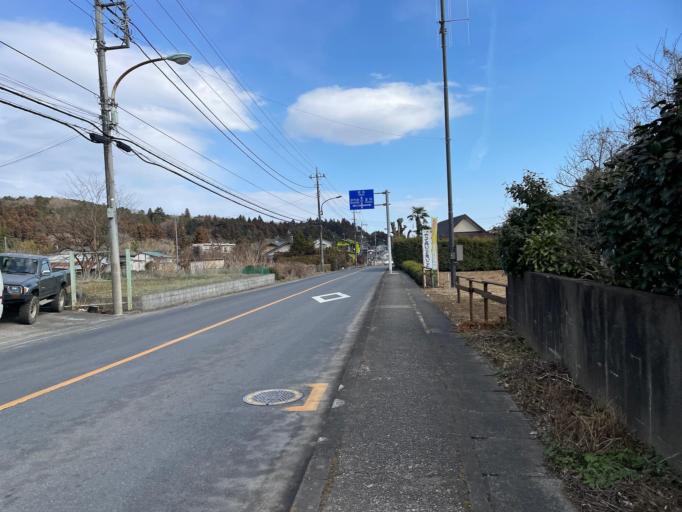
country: JP
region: Saitama
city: Hanno
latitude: 35.8376
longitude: 139.2789
